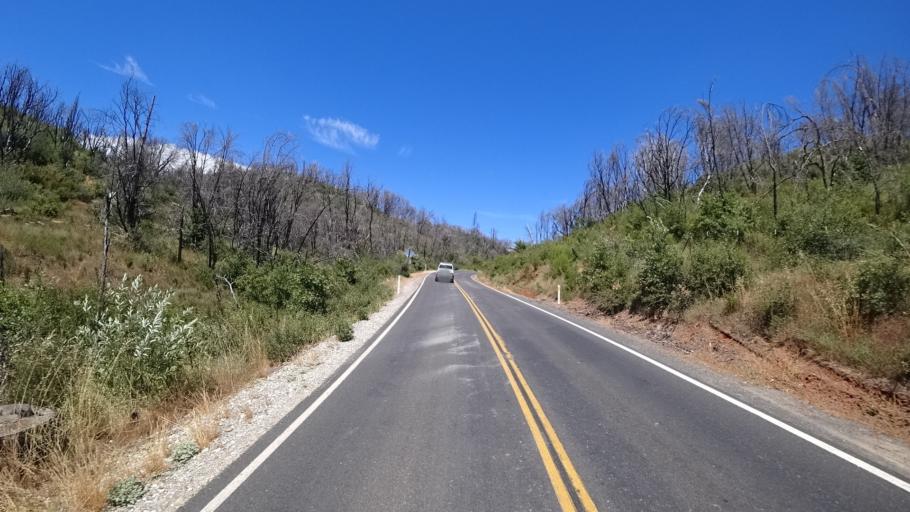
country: US
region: California
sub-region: Calaveras County
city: Mountain Ranch
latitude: 38.2372
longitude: -120.5198
